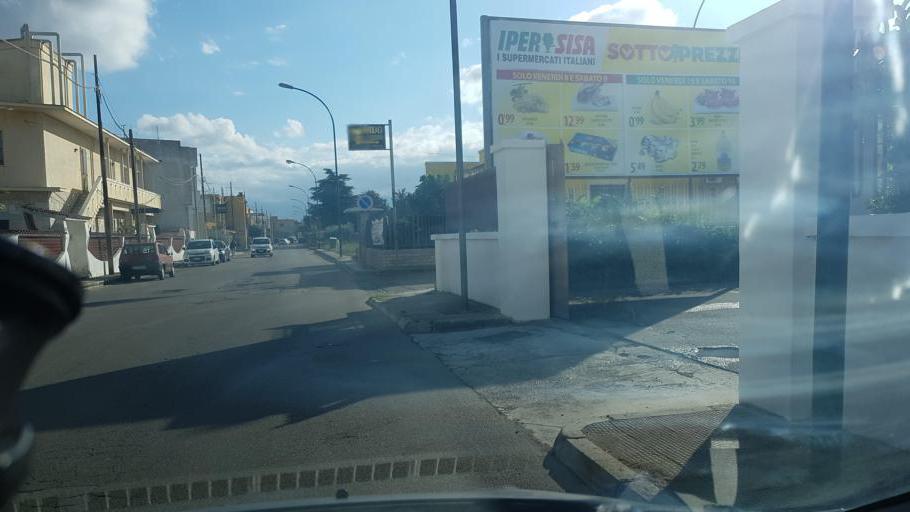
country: IT
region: Apulia
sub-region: Provincia di Lecce
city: Squinzano
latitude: 40.4352
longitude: 18.0318
